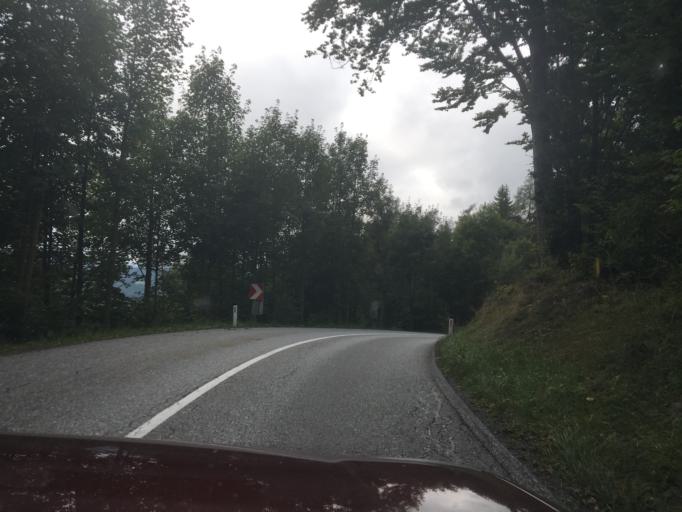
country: AT
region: Styria
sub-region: Politischer Bezirk Deutschlandsberg
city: Trahutten
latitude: 46.8246
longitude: 15.1479
